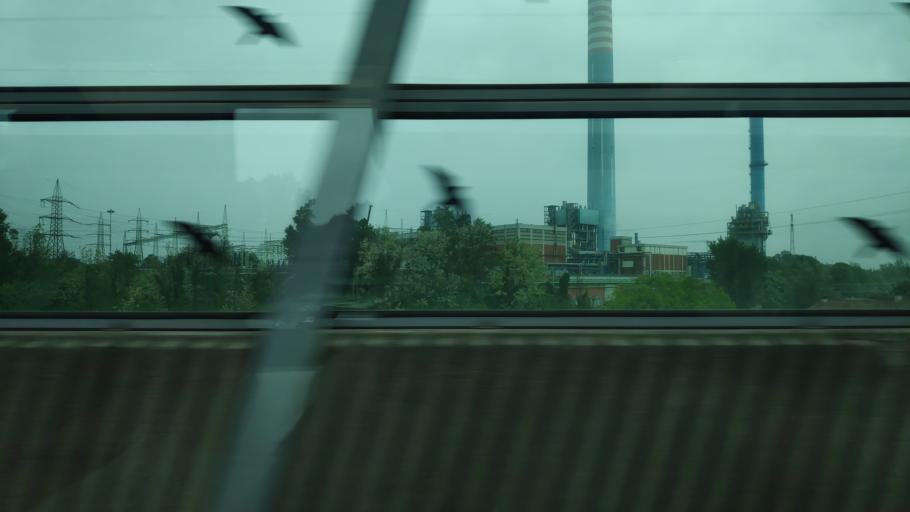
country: IT
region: Lombardy
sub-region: Citta metropolitana di Milano
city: Albignano
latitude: 45.5087
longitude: 9.5107
